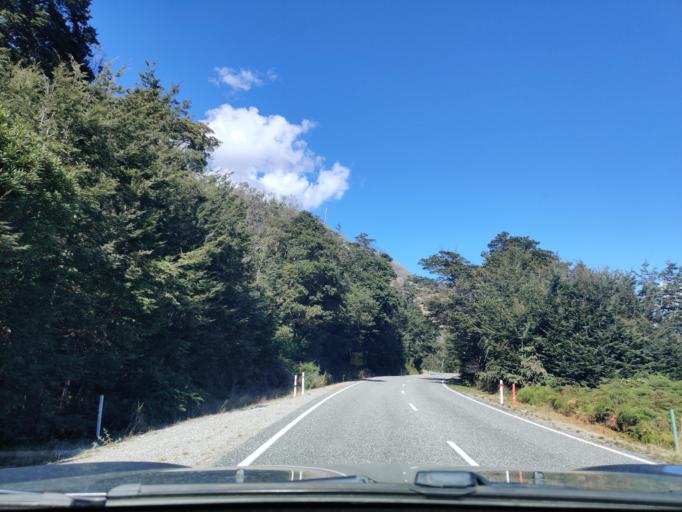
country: NZ
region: Otago
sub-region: Queenstown-Lakes District
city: Queenstown
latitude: -44.9961
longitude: 168.4349
